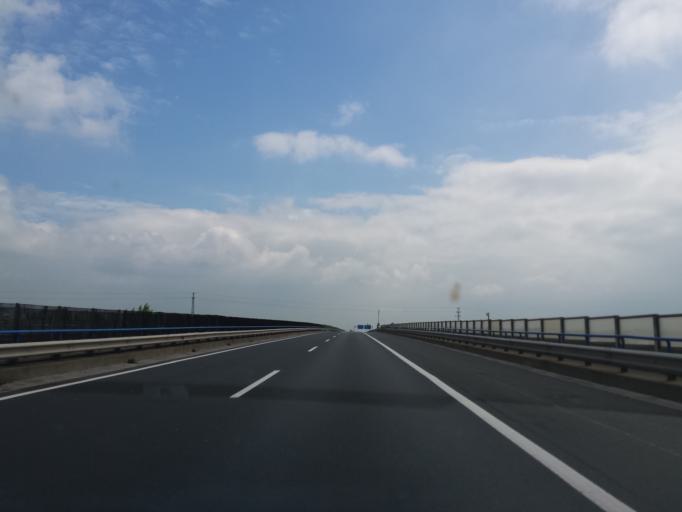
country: AT
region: Burgenland
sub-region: Politischer Bezirk Neusiedl am See
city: Nickelsdorf
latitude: 47.9044
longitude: 17.1542
